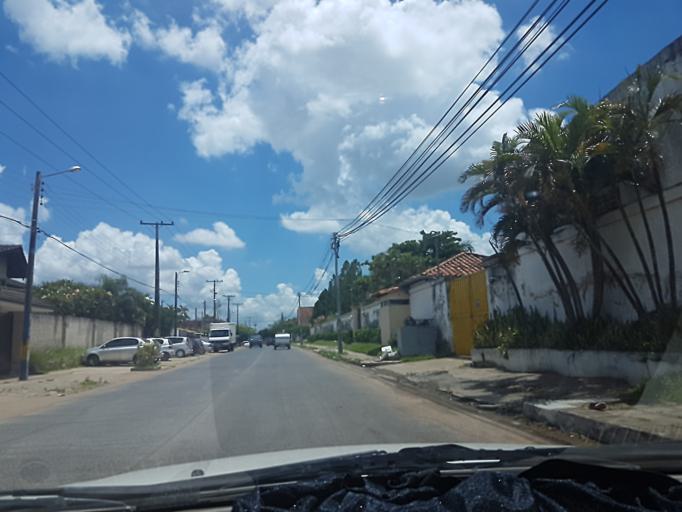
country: PY
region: Central
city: Fernando de la Mora
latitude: -25.2869
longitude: -57.5375
